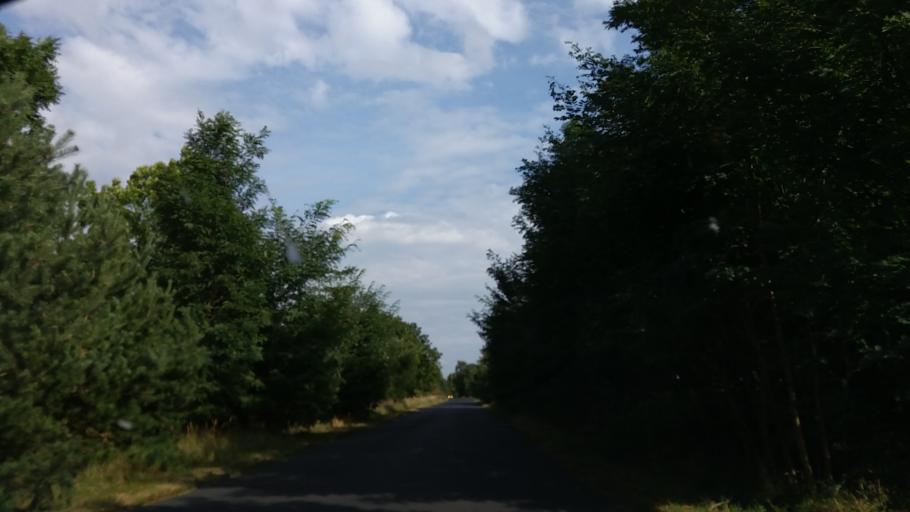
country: PL
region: West Pomeranian Voivodeship
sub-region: Powiat stargardzki
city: Suchan
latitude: 53.2240
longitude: 15.2866
